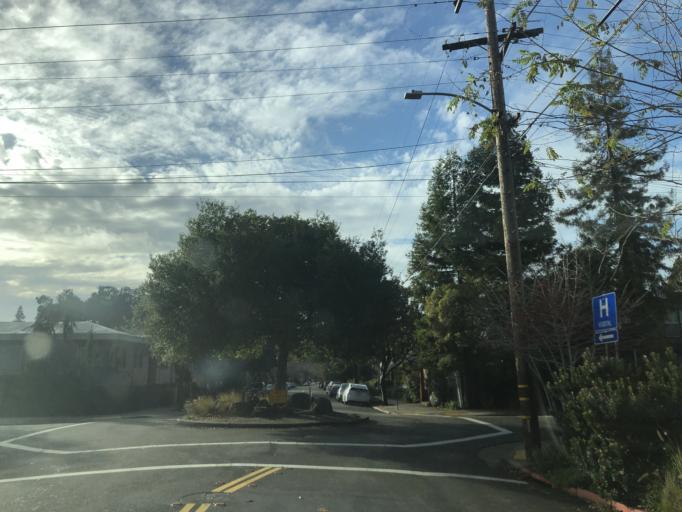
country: US
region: California
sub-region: Alameda County
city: Berkeley
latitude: 37.8536
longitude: -122.2559
